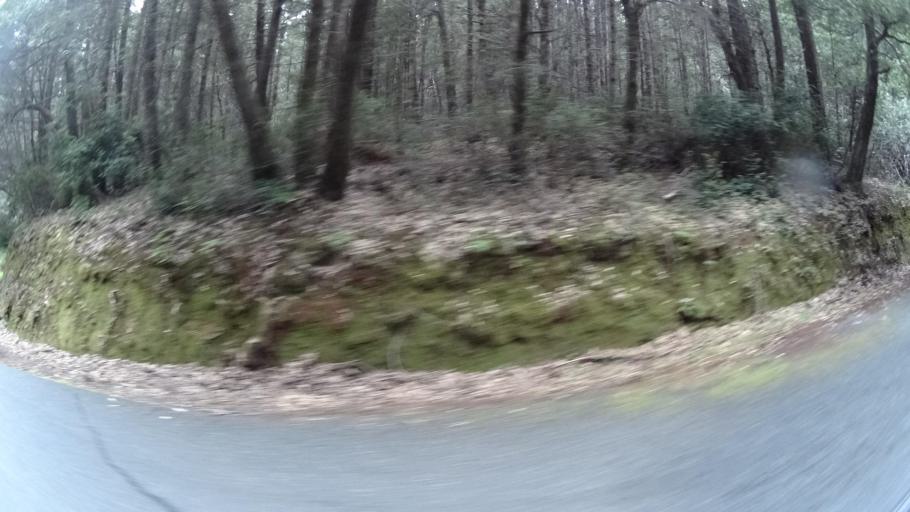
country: US
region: California
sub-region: Humboldt County
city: Willow Creek
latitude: 41.2003
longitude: -123.7639
